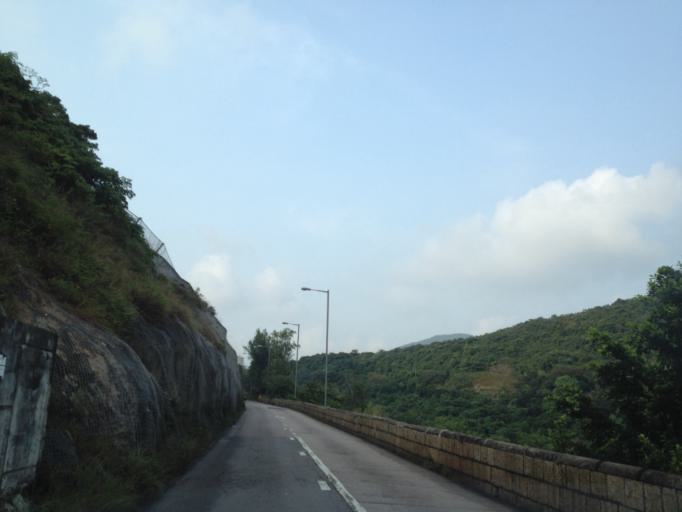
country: HK
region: Wanchai
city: Wan Chai
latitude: 22.2330
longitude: 114.2226
